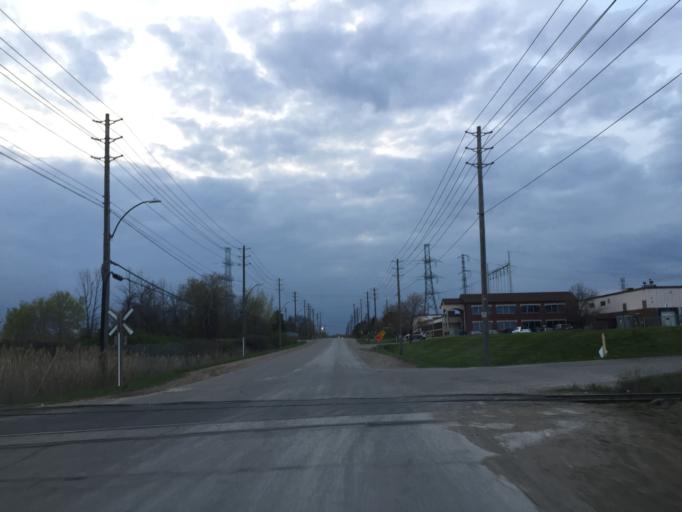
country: CA
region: Ontario
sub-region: Wellington County
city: Guelph
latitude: 43.5516
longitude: -80.2820
